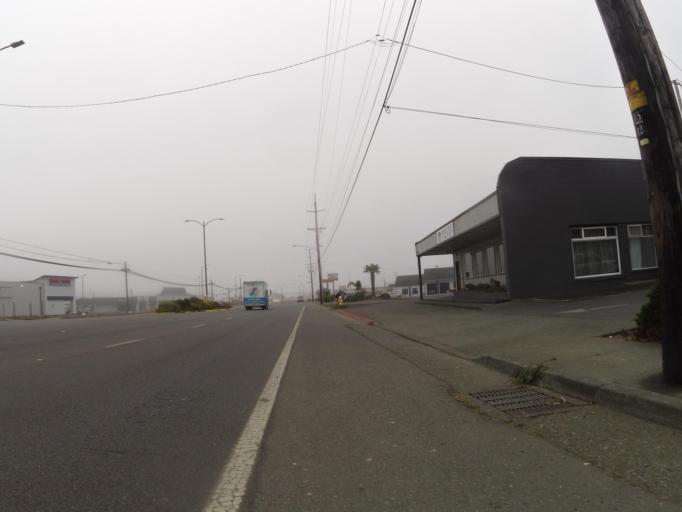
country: US
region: California
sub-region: Del Norte County
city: Crescent City
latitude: 41.7657
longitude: -124.1982
